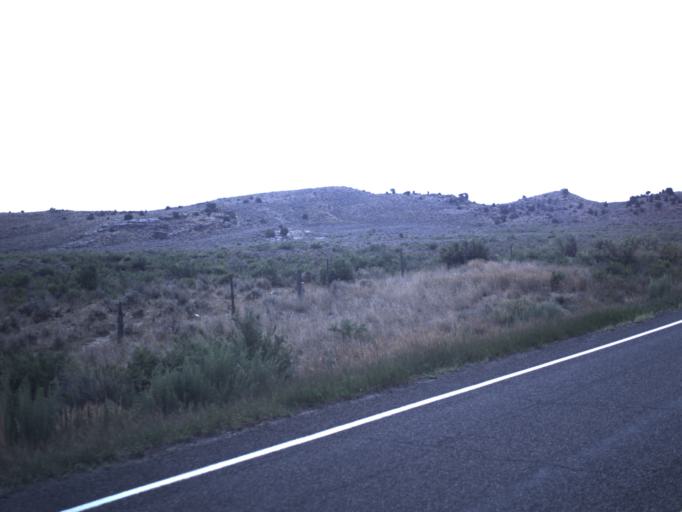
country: US
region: Utah
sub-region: Daggett County
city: Manila
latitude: 40.9635
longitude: -109.7130
